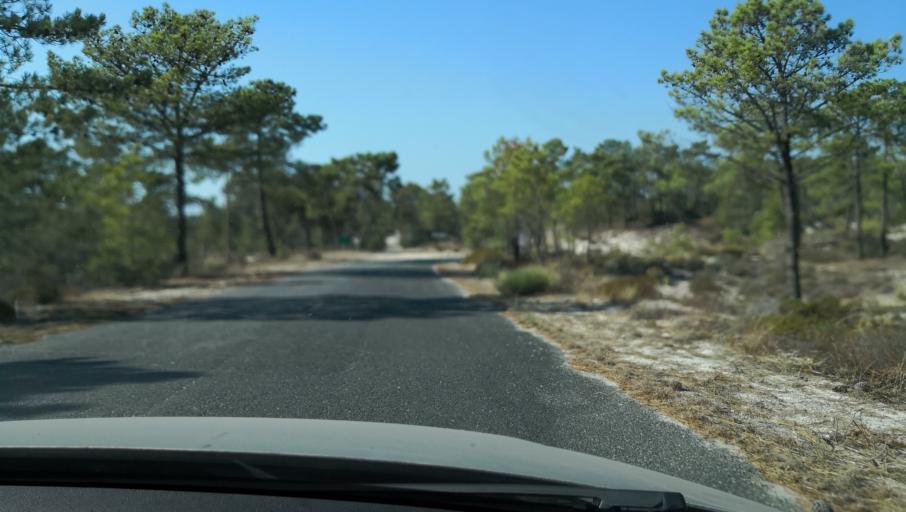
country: PT
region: Setubal
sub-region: Setubal
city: Setubal
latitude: 38.4724
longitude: -8.8736
